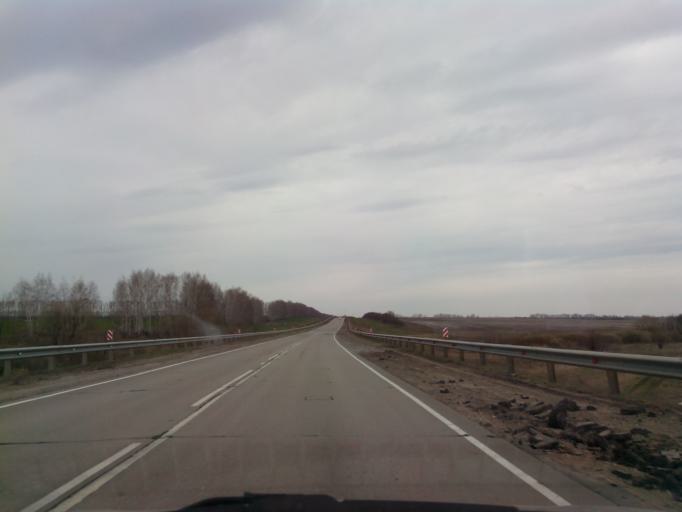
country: RU
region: Tambov
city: Znamenka
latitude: 52.4193
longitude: 41.3765
